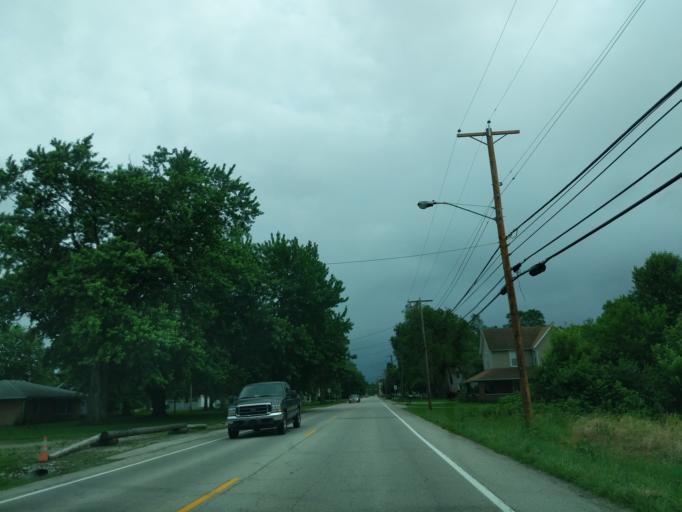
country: US
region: Indiana
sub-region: Delaware County
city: Daleville
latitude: 40.1267
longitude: -85.5532
